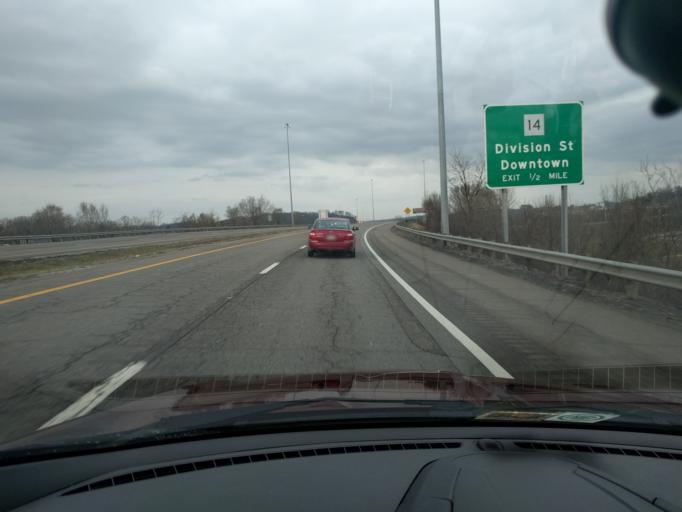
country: US
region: West Virginia
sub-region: Wood County
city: Parkersburg
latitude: 39.2545
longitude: -81.5433
